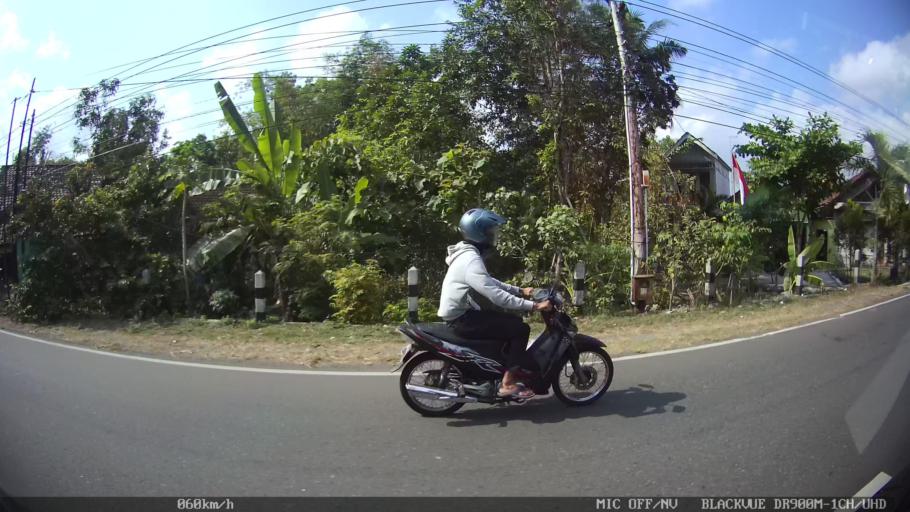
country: ID
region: Daerah Istimewa Yogyakarta
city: Srandakan
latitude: -7.8570
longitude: 110.2135
